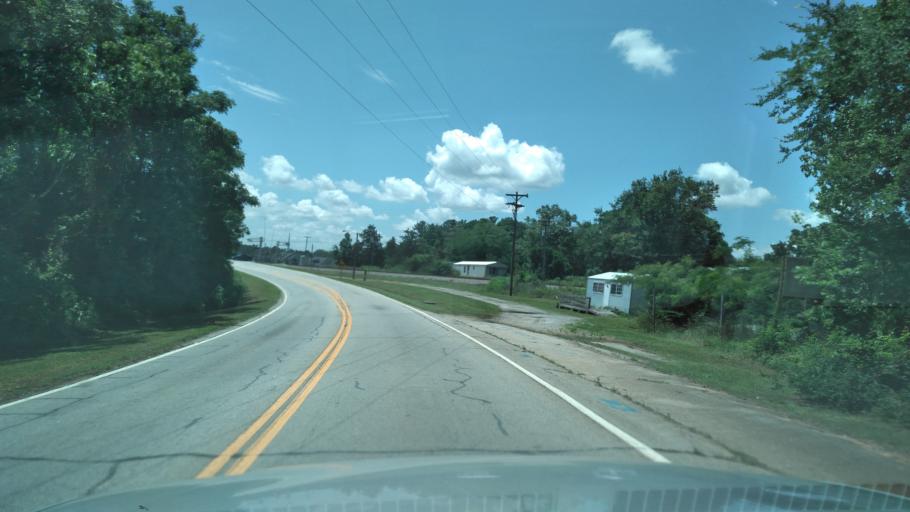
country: US
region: South Carolina
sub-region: Laurens County
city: Laurens
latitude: 34.3474
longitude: -82.0614
